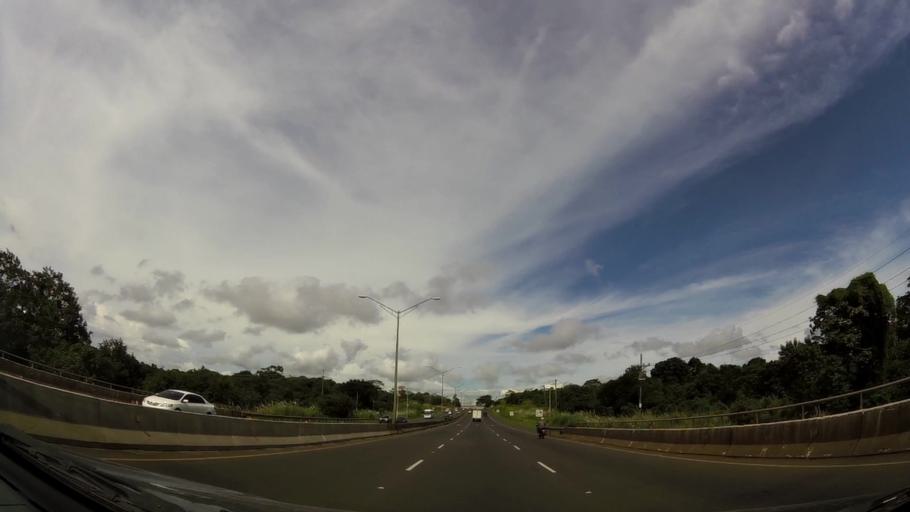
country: PA
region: Panama
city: La Chorrera
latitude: 8.8866
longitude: -79.7541
